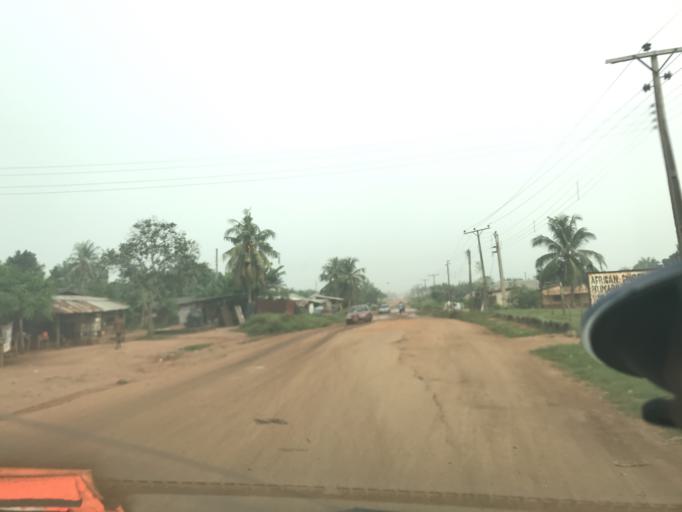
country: NG
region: Ogun
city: Ado Odo
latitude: 6.5294
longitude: 2.9512
